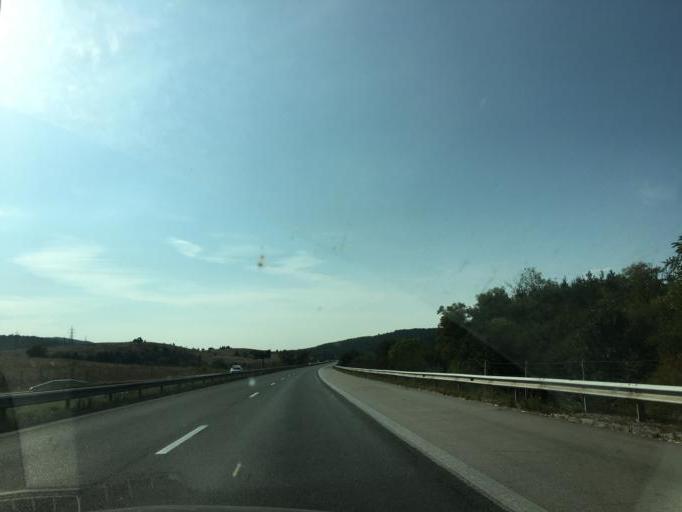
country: BG
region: Sofiya
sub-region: Obshtina Ikhtiman
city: Ikhtiman
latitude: 42.5230
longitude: 23.7484
